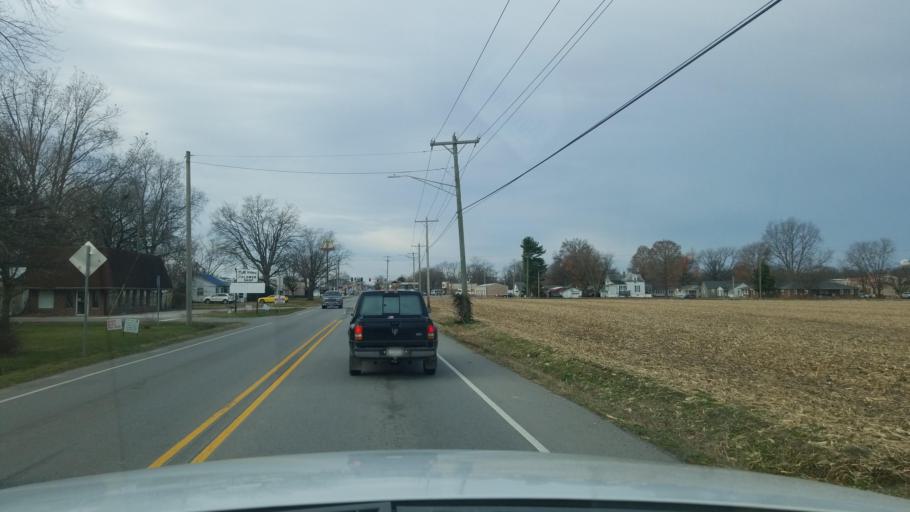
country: US
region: Indiana
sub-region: Posey County
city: Mount Vernon
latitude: 37.9360
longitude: -87.8809
